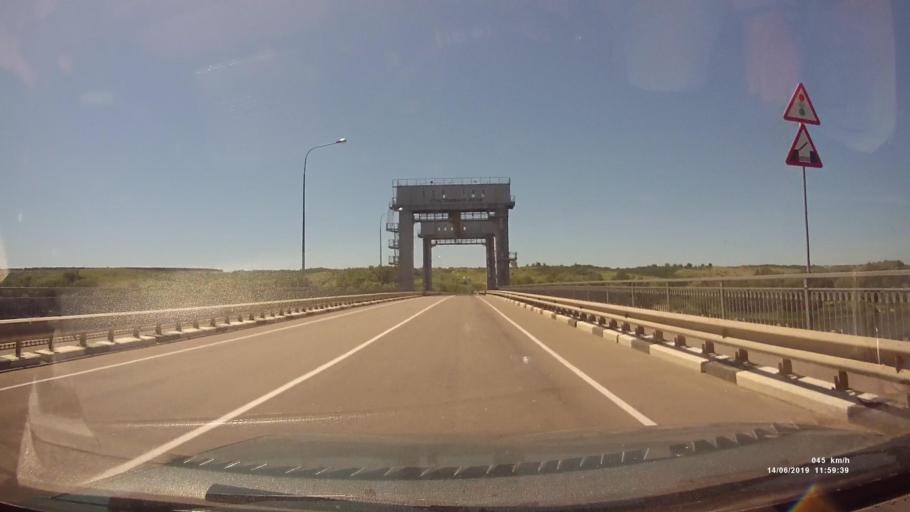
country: RU
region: Rostov
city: Kazanskaya
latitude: 49.7916
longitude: 41.1347
